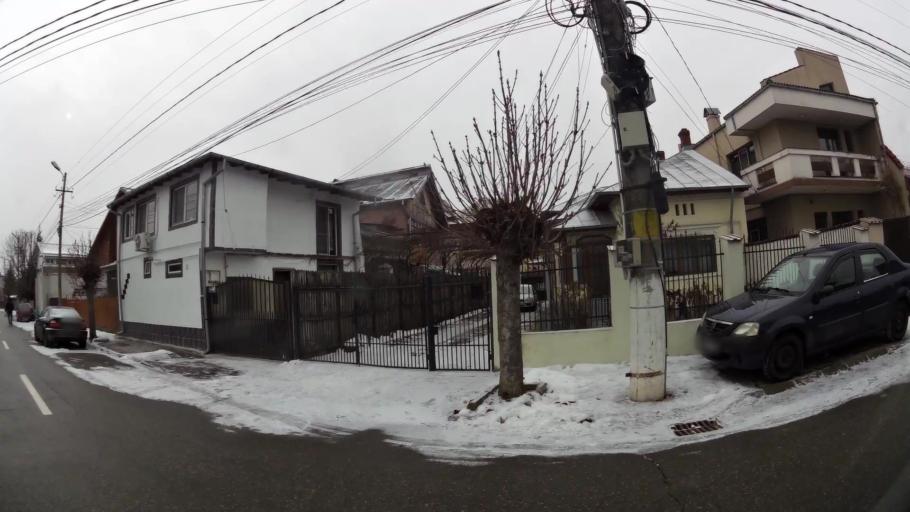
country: RO
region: Dambovita
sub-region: Municipiul Targoviste
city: Targoviste
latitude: 44.9367
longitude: 25.4527
